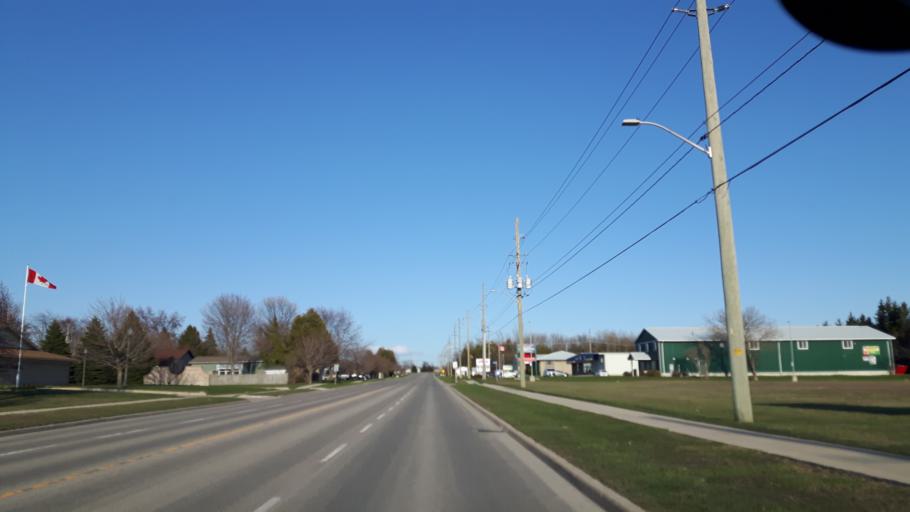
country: CA
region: Ontario
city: Goderich
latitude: 43.7316
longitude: -81.7021
